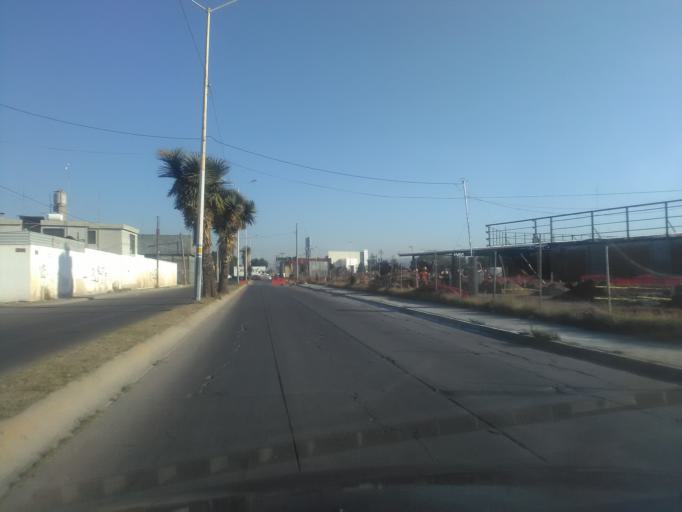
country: MX
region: Durango
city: Victoria de Durango
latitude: 24.0454
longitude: -104.6230
